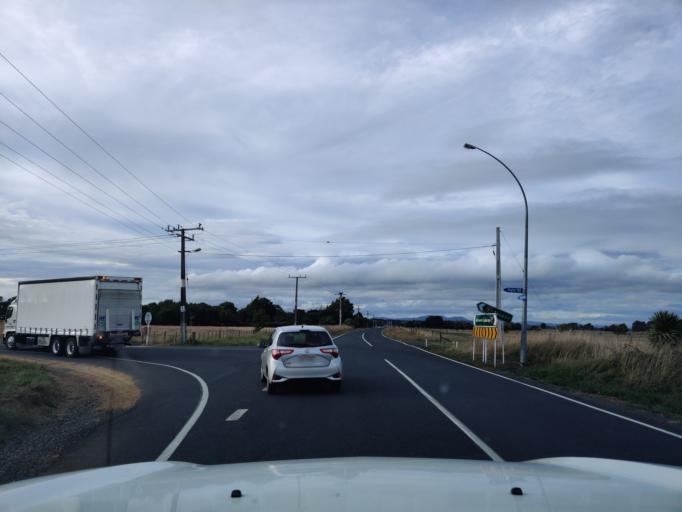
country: NZ
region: Waikato
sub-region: Hamilton City
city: Hamilton
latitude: -37.6870
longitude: 175.3383
